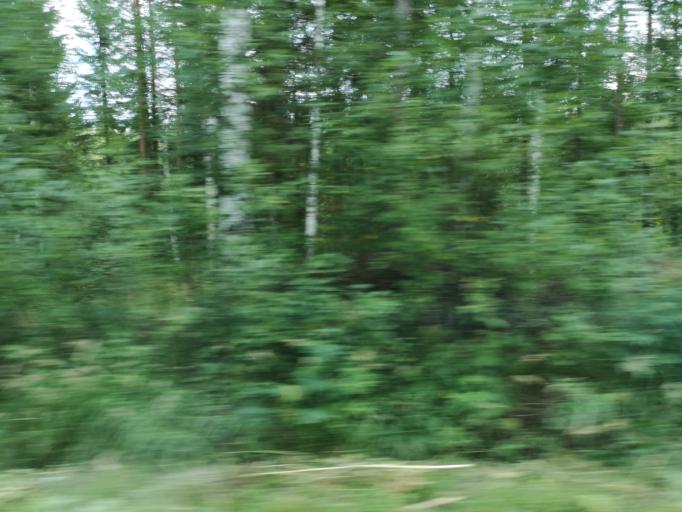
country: FI
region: Central Finland
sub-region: Jyvaeskylae
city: Hankasalmi
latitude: 62.4303
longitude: 26.6557
